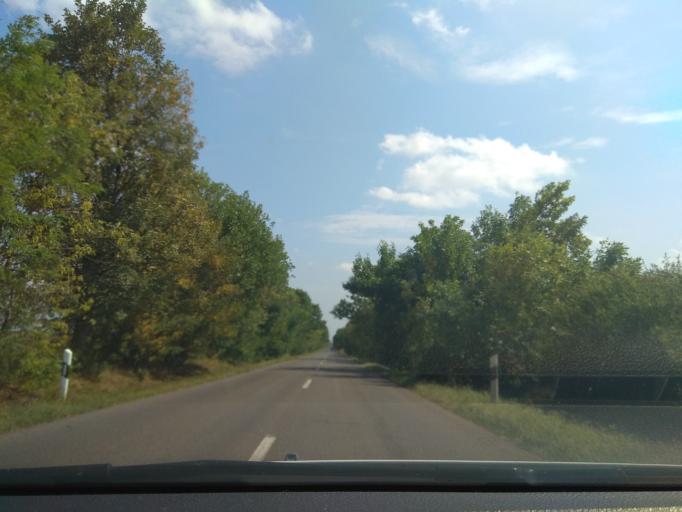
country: HU
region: Heves
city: Ostoros
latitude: 47.8256
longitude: 20.4738
